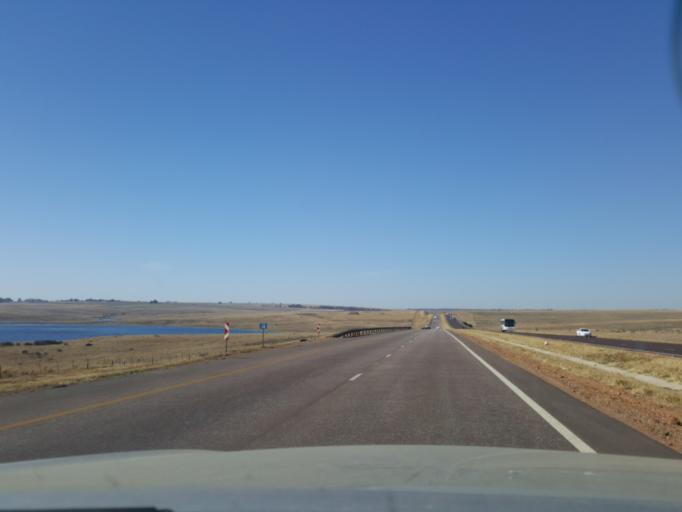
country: ZA
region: Mpumalanga
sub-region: Nkangala District Municipality
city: Middelburg
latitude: -25.8223
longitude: 29.5699
